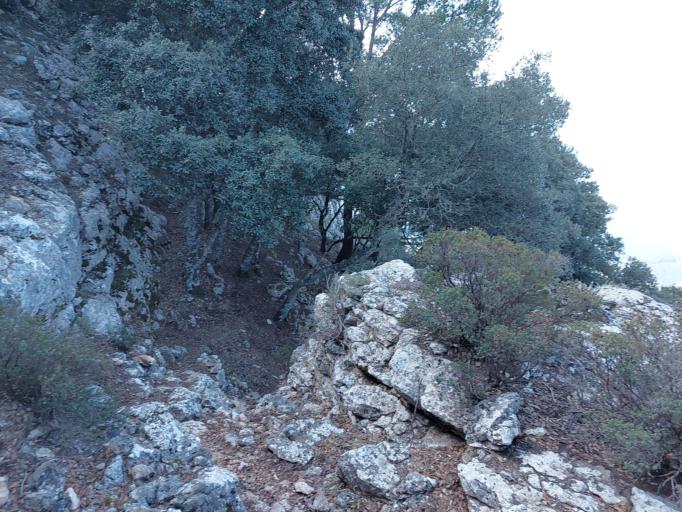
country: ES
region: Balearic Islands
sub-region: Illes Balears
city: Estellencs
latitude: 39.6569
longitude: 2.5082
